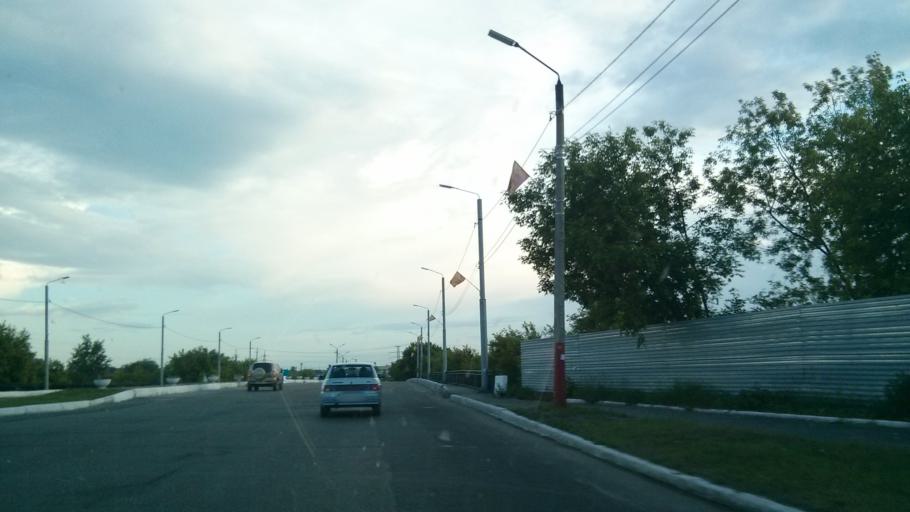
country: RU
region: Vladimir
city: Murom
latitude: 55.5645
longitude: 42.0613
